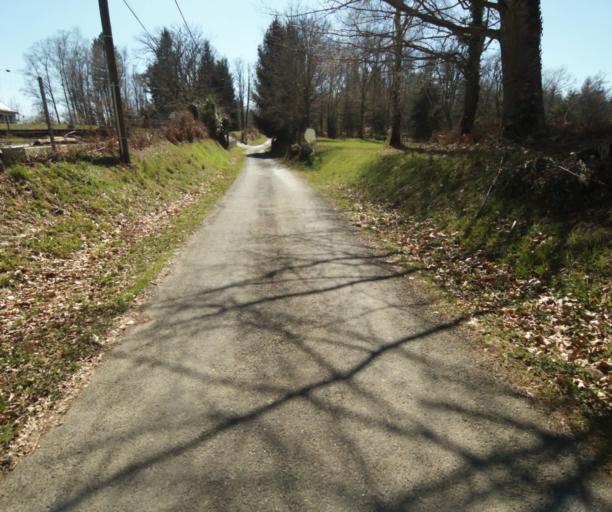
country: FR
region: Limousin
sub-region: Departement de la Correze
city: Chameyrat
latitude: 45.2748
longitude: 1.7044
